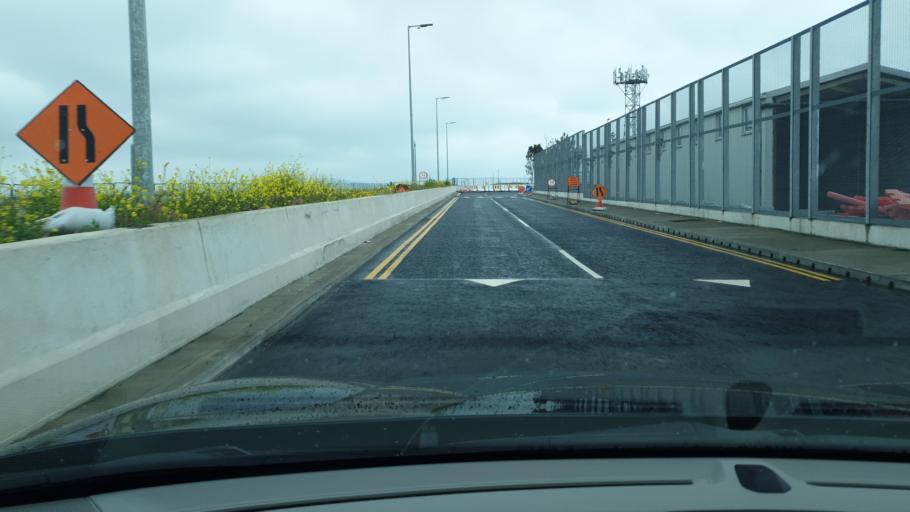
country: IE
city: Killester
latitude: 53.3531
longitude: -6.1988
